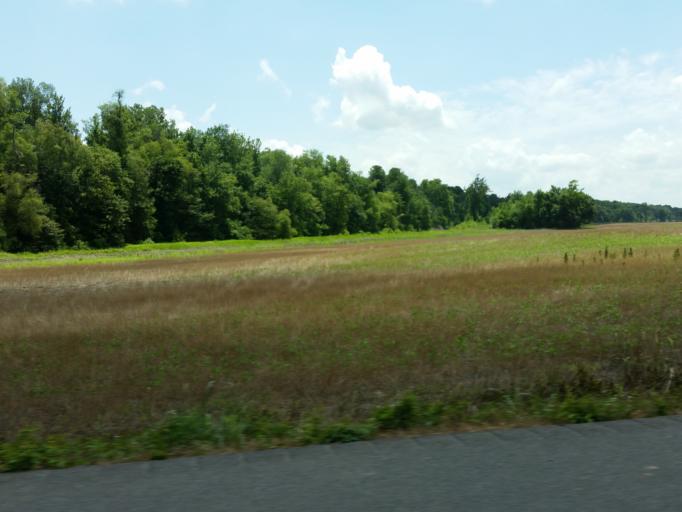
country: US
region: Kentucky
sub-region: Fulton County
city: Hickman
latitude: 36.5099
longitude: -89.3497
